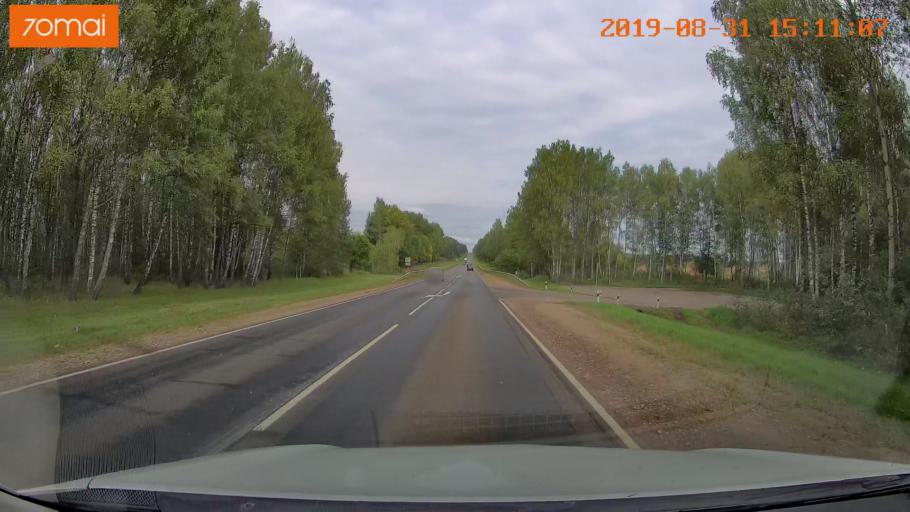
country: RU
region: Kaluga
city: Spas-Demensk
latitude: 54.4197
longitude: 34.2358
